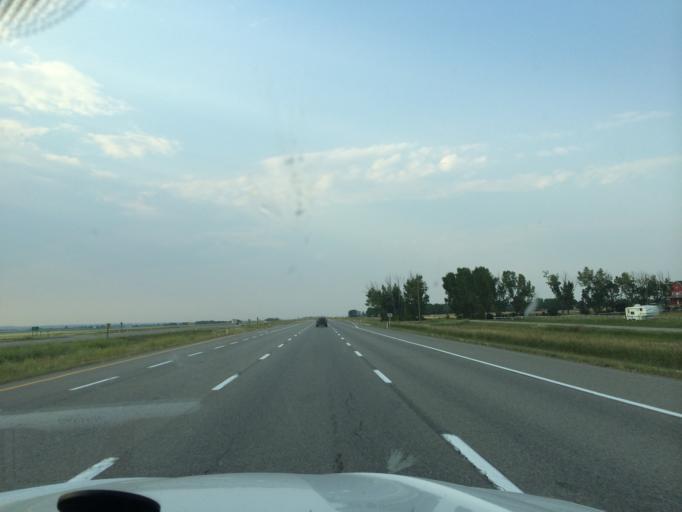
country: CA
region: Alberta
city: High River
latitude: 50.6284
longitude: -113.8363
